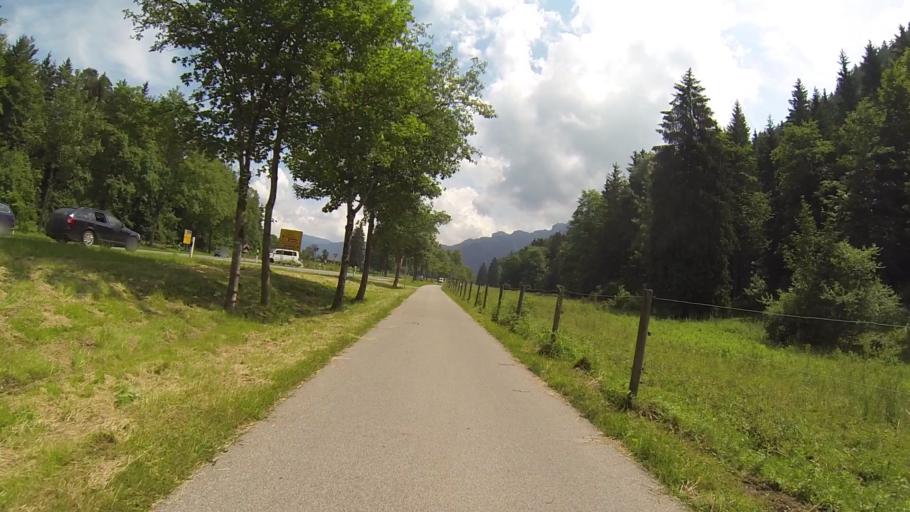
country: DE
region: Bavaria
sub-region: Swabia
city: Fuessen
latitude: 47.5652
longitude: 10.7152
